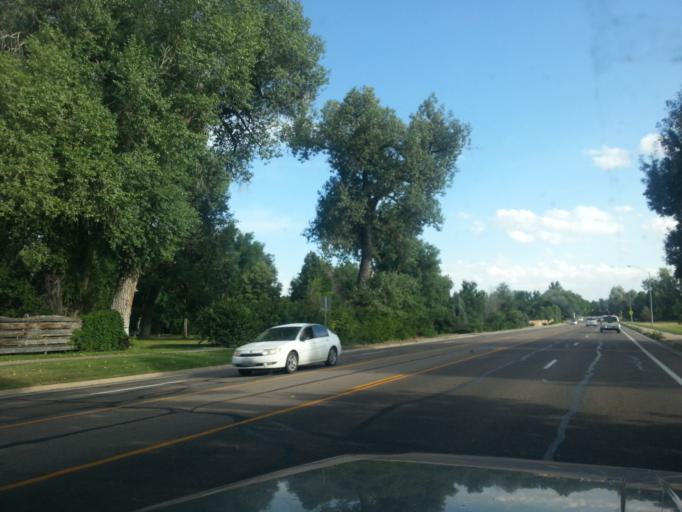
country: US
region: Colorado
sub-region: Larimer County
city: Fort Collins
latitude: 40.5443
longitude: -105.0581
